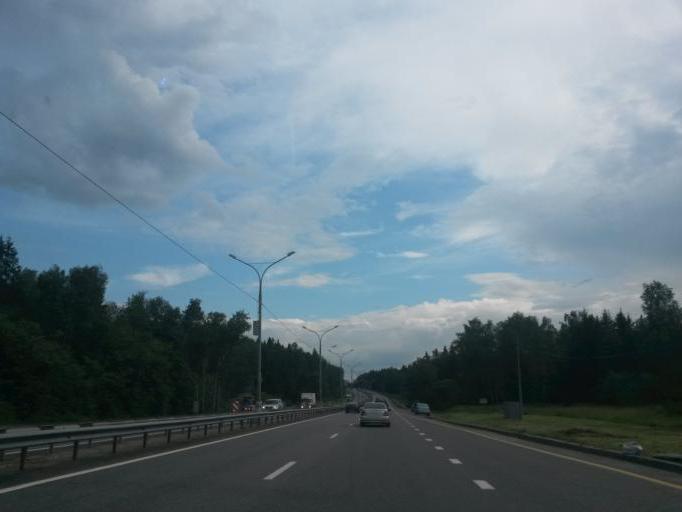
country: RU
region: Moskovskaya
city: Vostryakovo
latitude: 55.4640
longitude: 37.8538
